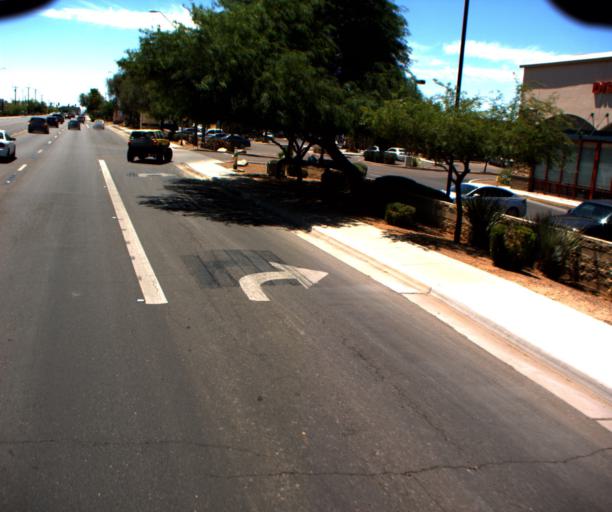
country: US
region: Arizona
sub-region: Pinal County
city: Casa Grande
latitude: 32.8796
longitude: -111.7192
